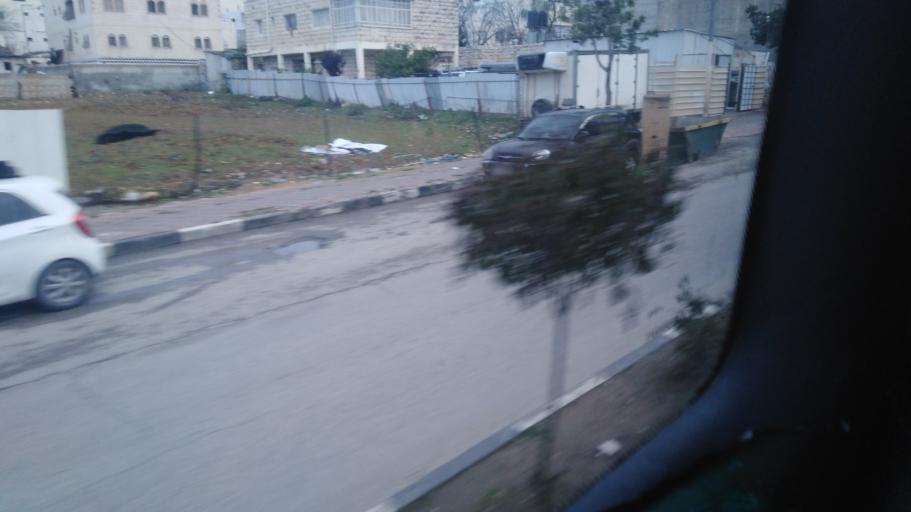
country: PS
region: West Bank
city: Hebron
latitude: 31.5308
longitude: 35.0907
